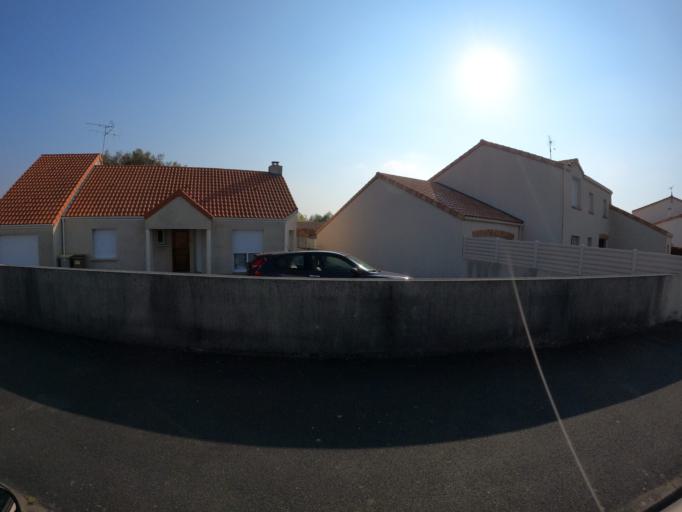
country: FR
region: Pays de la Loire
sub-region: Departement de Maine-et-Loire
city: La Seguiniere
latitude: 47.0577
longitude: -0.9381
